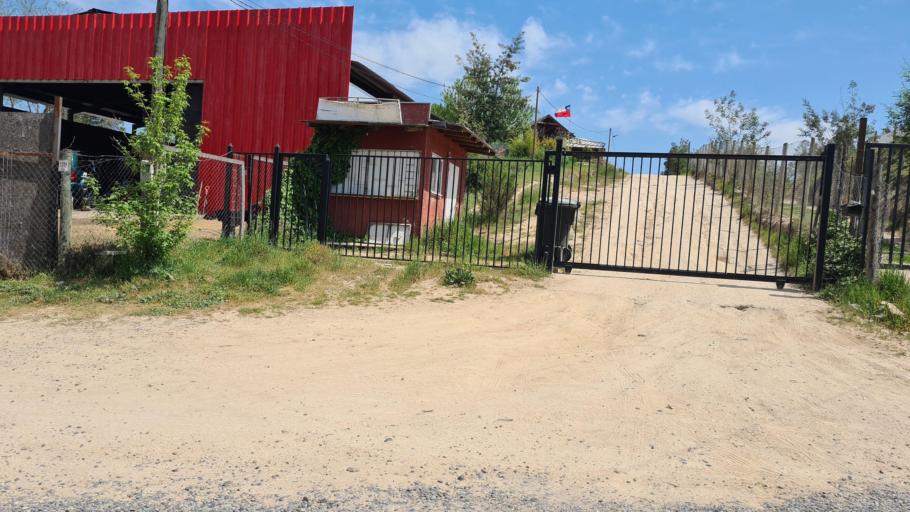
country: CL
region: O'Higgins
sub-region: Provincia de Cachapoal
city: San Vicente
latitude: -34.1635
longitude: -71.4091
